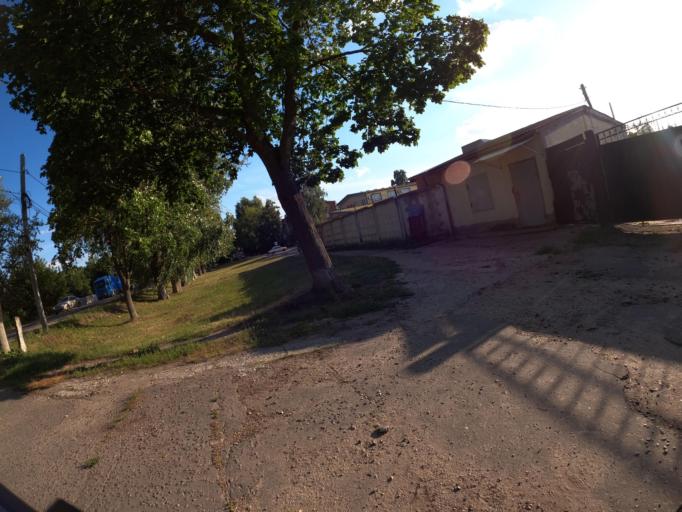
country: RU
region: Moskovskaya
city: Raduzhnyy
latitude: 55.1389
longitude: 38.7312
